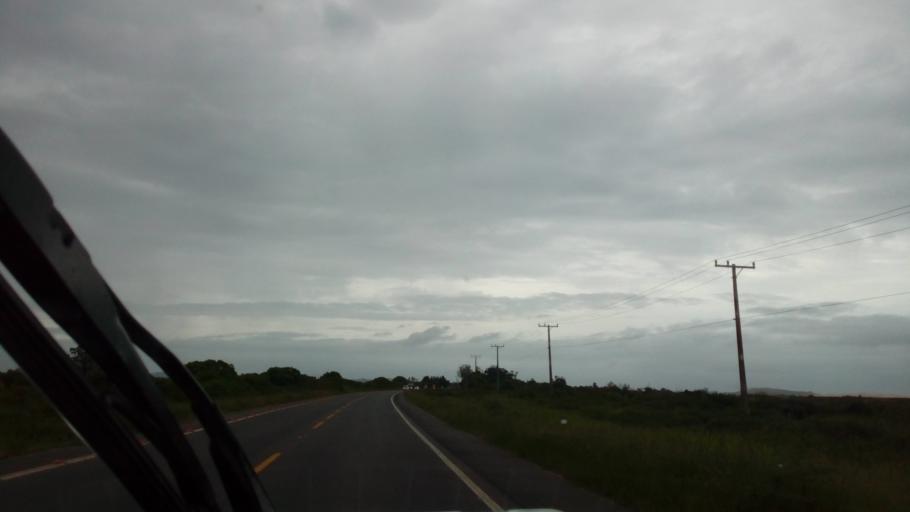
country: BR
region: Santa Catarina
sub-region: Laguna
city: Laguna
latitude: -28.5801
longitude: -48.8263
